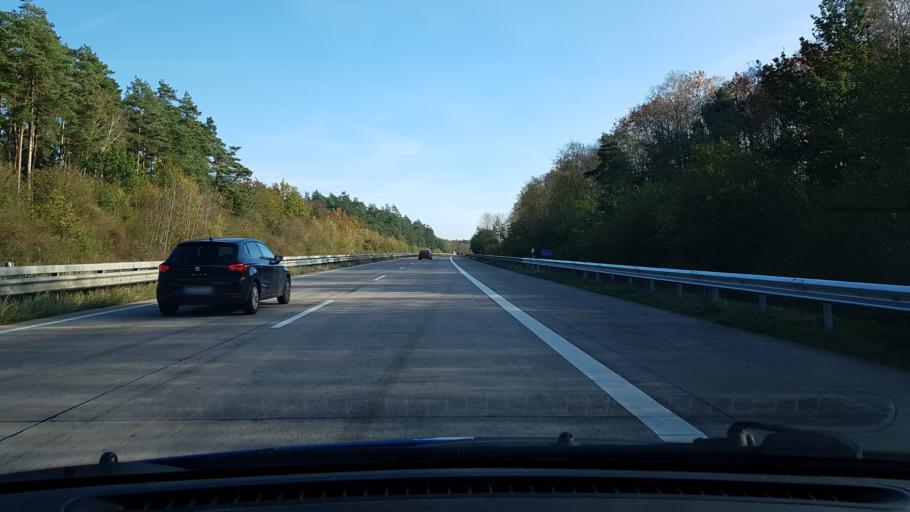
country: DE
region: Schleswig-Holstein
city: Guster
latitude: 53.5482
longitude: 10.6950
